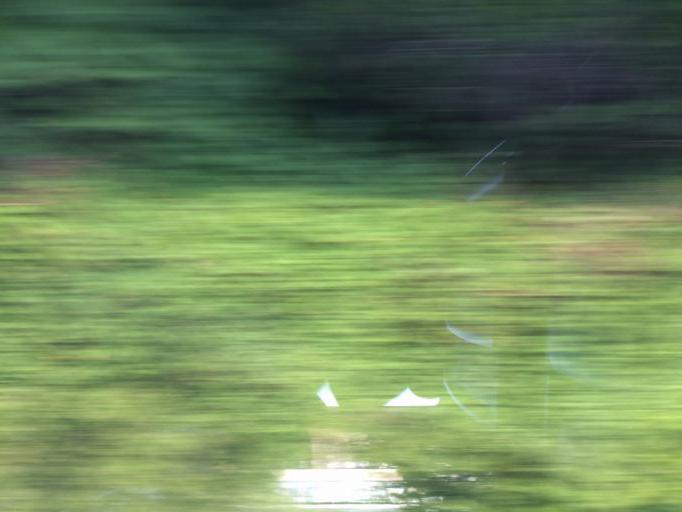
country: DE
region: North Rhine-Westphalia
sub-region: Regierungsbezirk Dusseldorf
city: Dusseldorf
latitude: 51.2756
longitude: 6.7891
